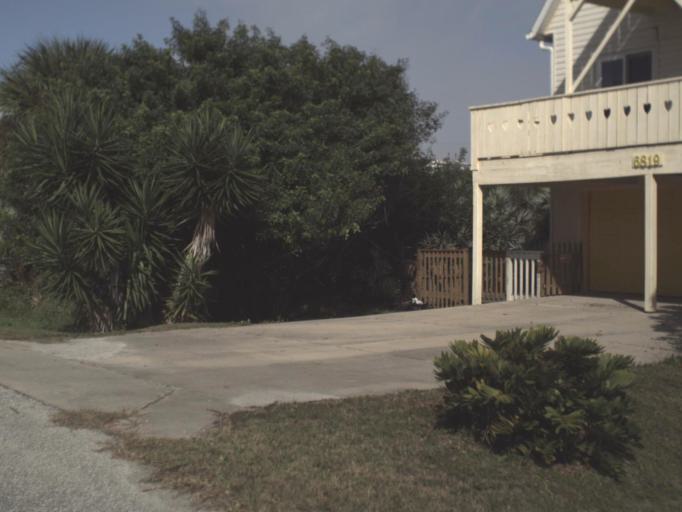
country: US
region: Florida
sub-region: Volusia County
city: Edgewater
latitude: 28.9464
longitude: -80.8370
